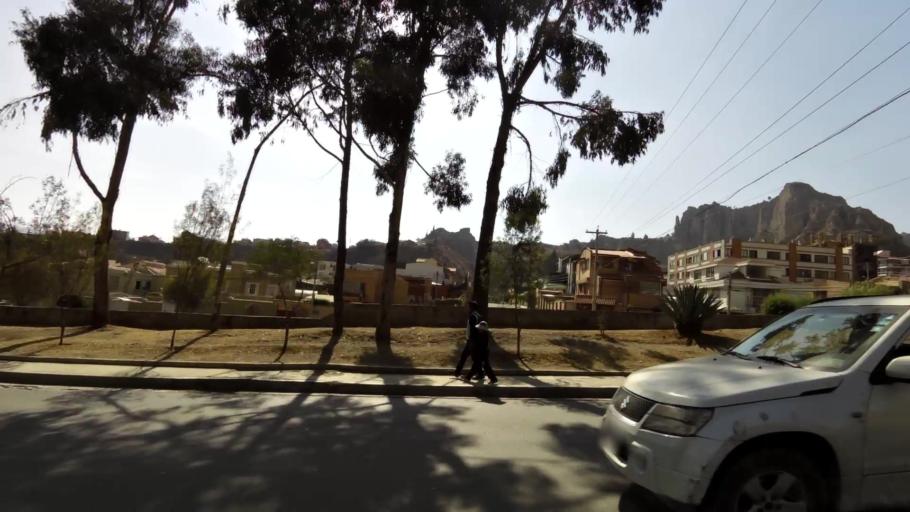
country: BO
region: La Paz
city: La Paz
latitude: -16.5276
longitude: -68.0700
